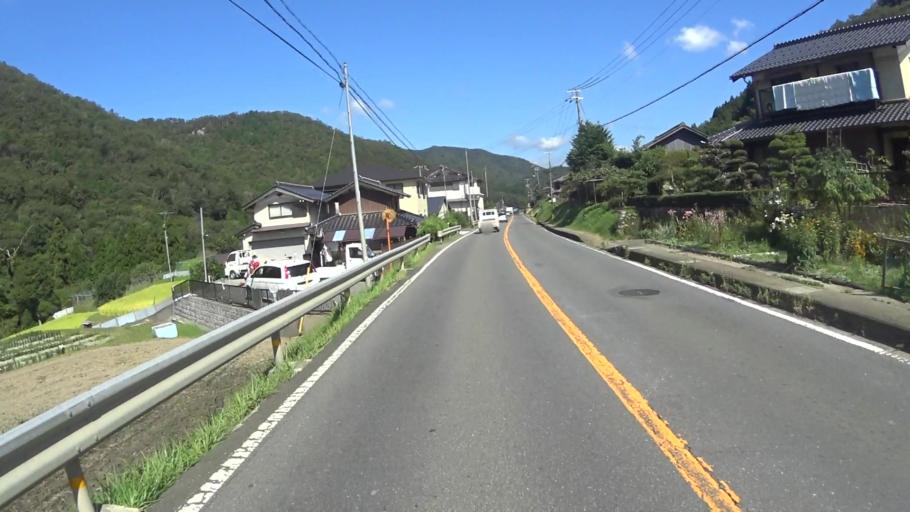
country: JP
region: Kyoto
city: Ayabe
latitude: 35.2328
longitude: 135.4138
